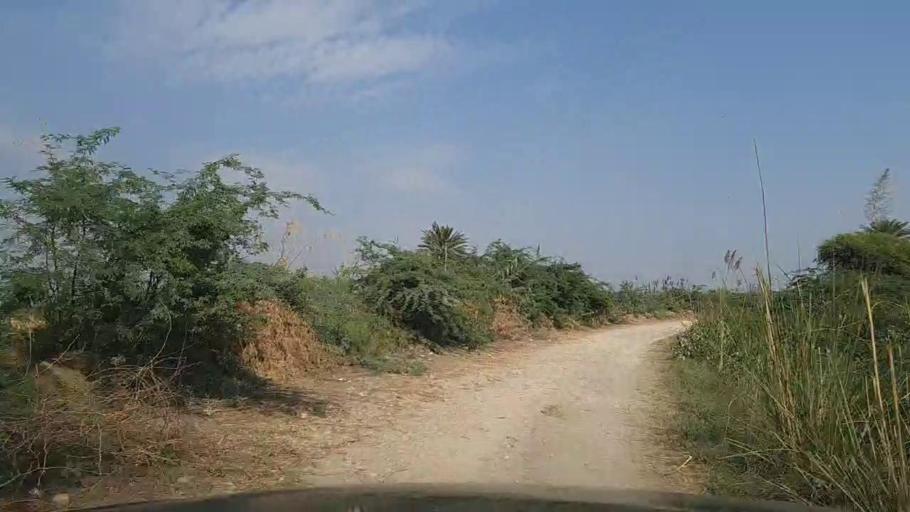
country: PK
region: Sindh
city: Thatta
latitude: 24.7692
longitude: 67.7726
